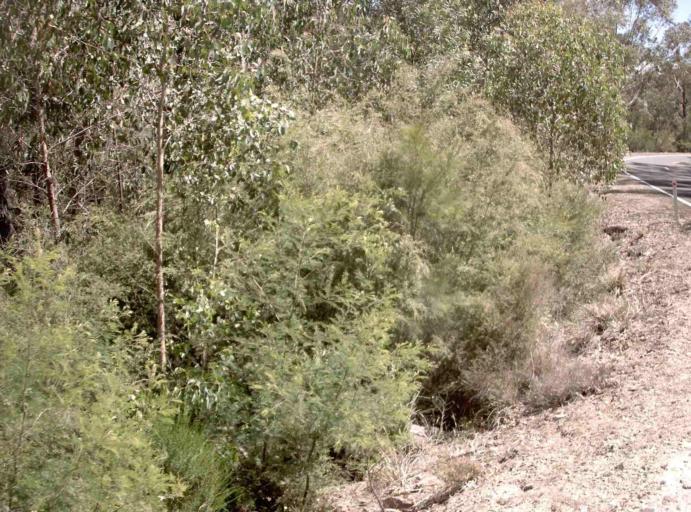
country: AU
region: Victoria
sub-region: East Gippsland
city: Lakes Entrance
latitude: -37.3735
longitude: 148.2190
